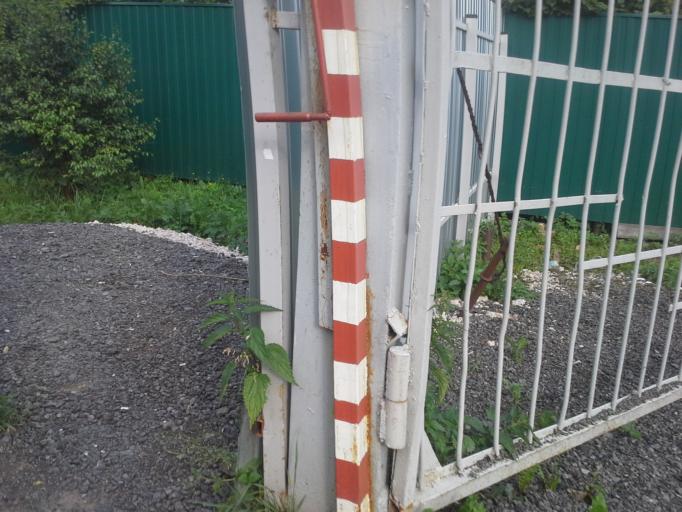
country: RU
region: Moskovskaya
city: Kievskij
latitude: 55.4456
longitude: 36.8248
